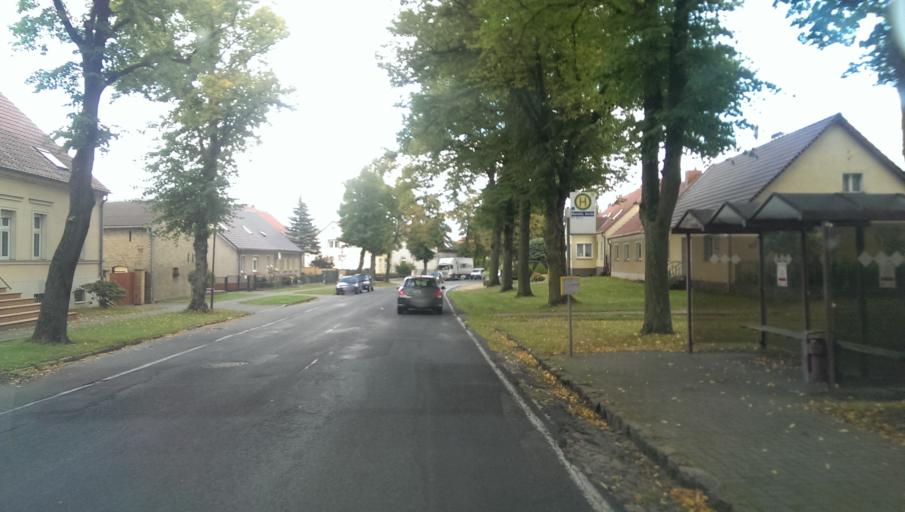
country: DE
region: Brandenburg
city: Velten
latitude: 52.6769
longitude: 13.1390
